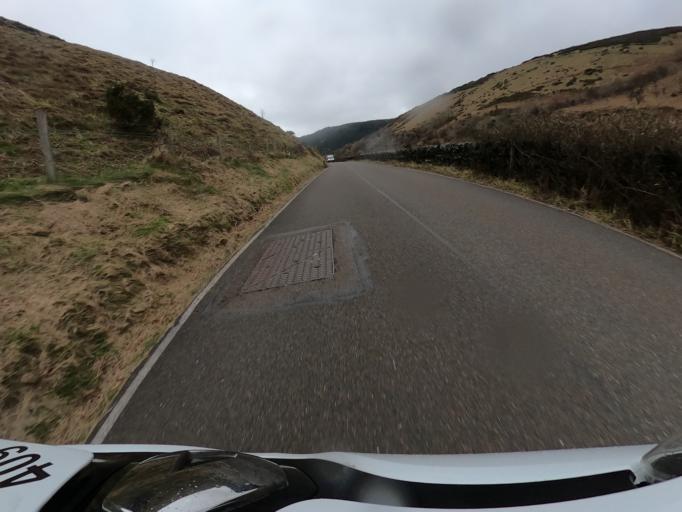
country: IM
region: Ramsey
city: Ramsey
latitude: 54.2925
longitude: -4.4892
